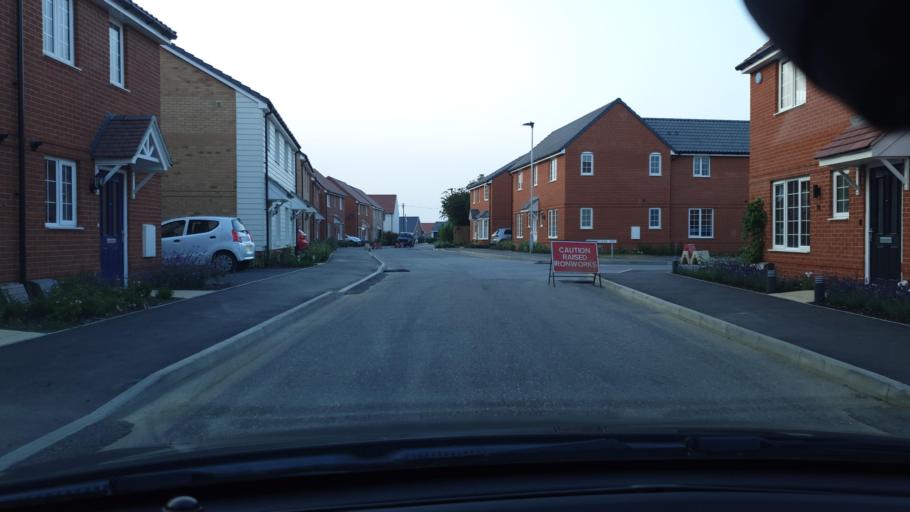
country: GB
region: England
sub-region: Essex
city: Frinton-on-Sea
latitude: 51.8435
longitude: 1.2040
